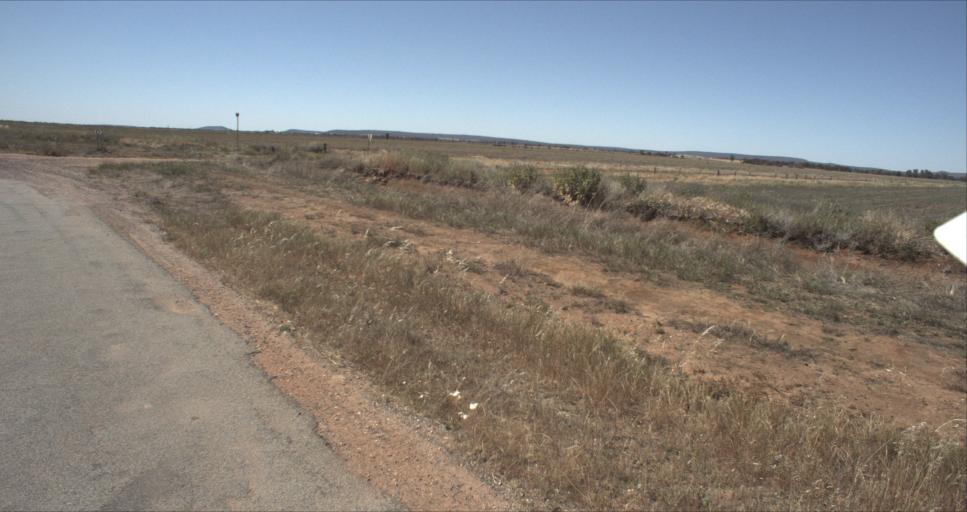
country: AU
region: New South Wales
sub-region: Leeton
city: Leeton
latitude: -34.5017
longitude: 146.3441
